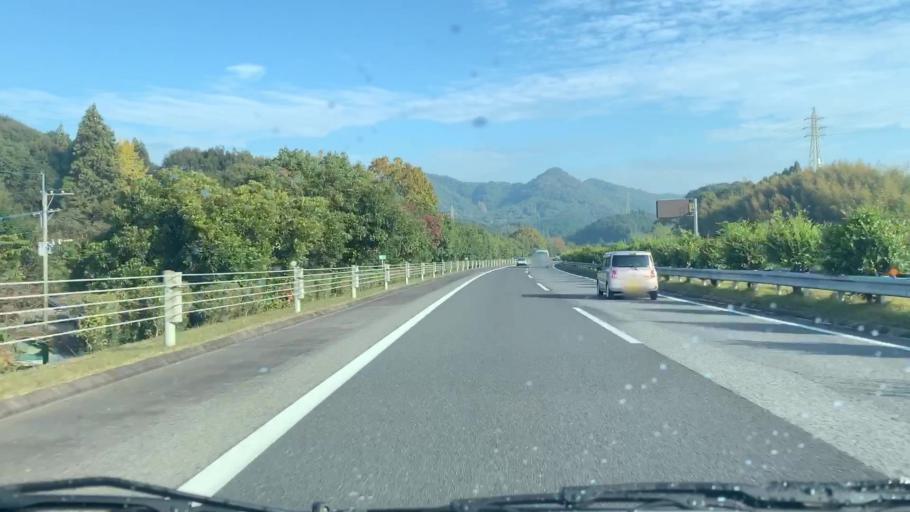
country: JP
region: Saga Prefecture
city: Takeocho-takeo
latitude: 33.2242
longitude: 130.0500
